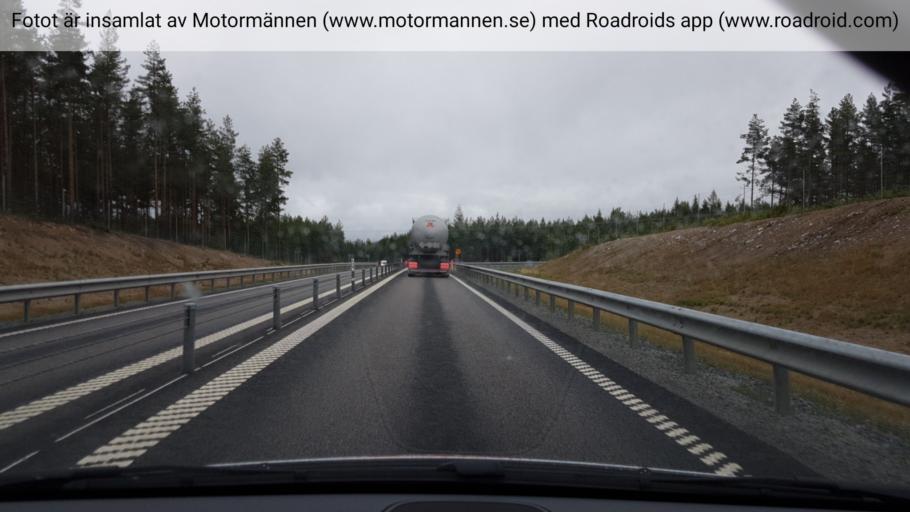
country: SE
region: Uppsala
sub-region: Heby Kommun
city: Heby
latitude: 59.9758
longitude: 16.8467
